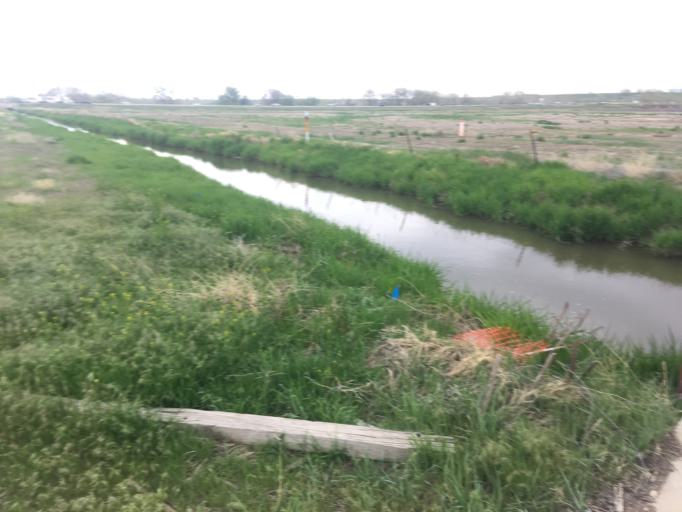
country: US
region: Colorado
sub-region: Weld County
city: Mead
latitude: 40.1706
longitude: -104.9749
